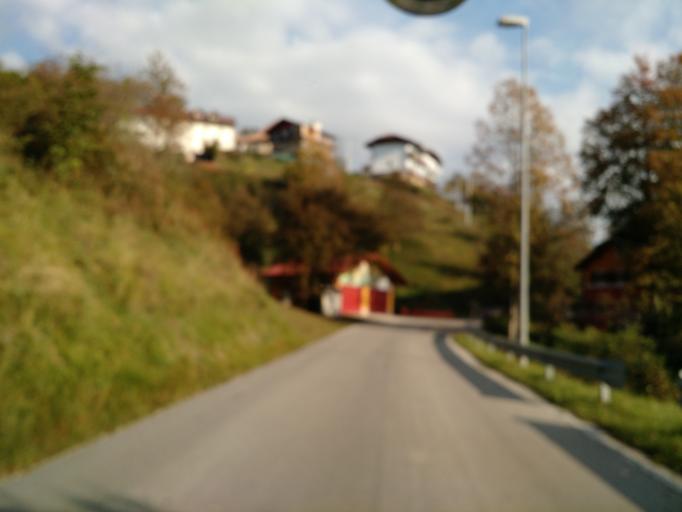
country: IT
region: Veneto
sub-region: Provincia di Vicenza
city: Foza
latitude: 45.8752
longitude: 11.6113
